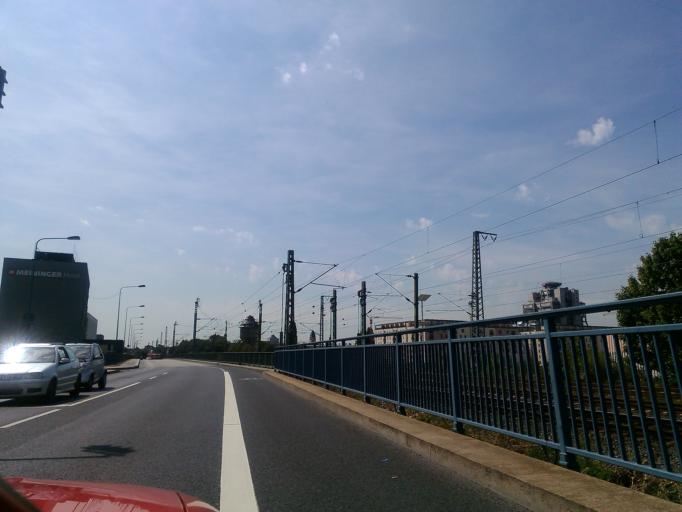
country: DE
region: Hesse
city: Niederrad
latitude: 50.1102
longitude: 8.6436
